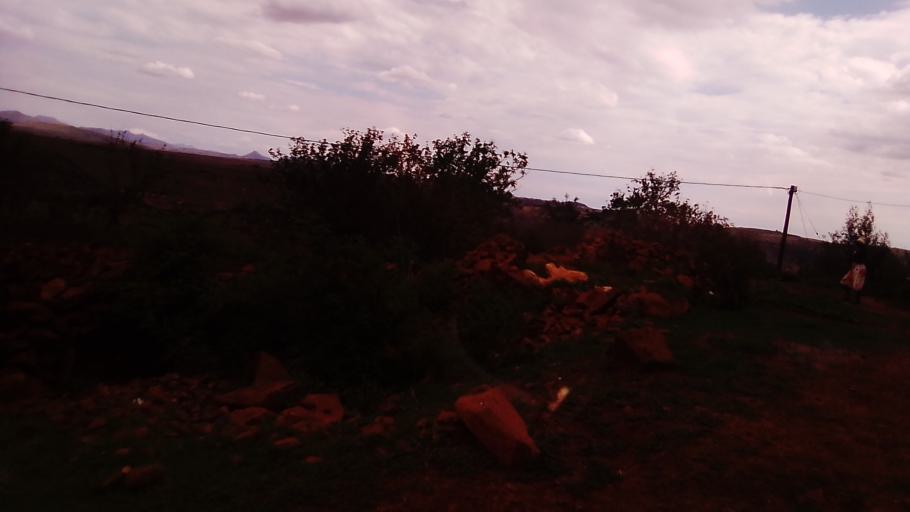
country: LS
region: Berea
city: Teyateyaneng
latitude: -29.3347
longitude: 27.7020
